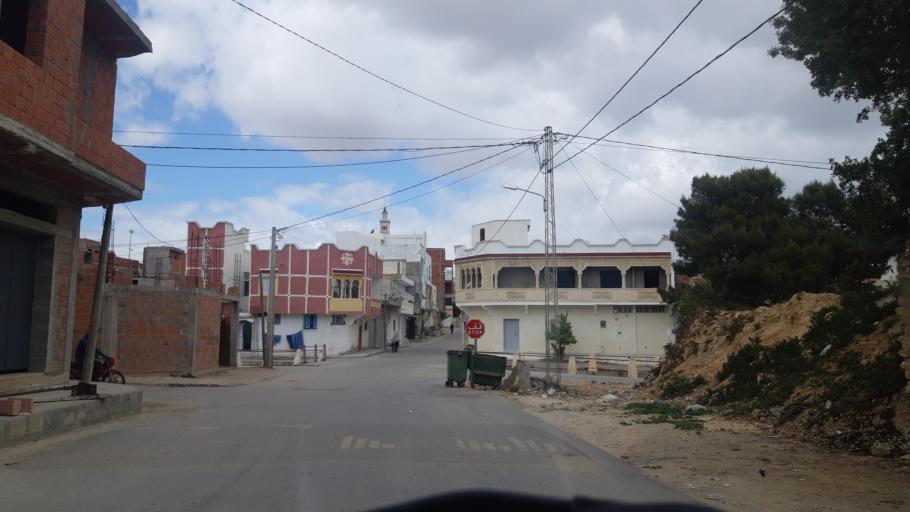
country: TN
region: Susah
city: Akouda
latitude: 35.8669
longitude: 10.5364
